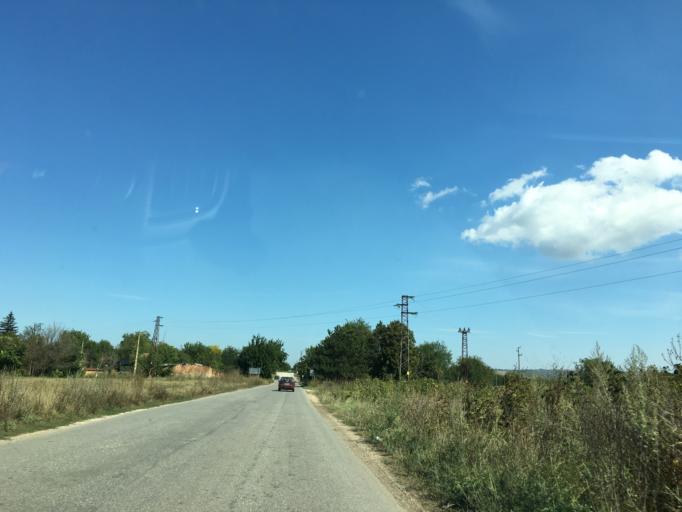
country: RO
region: Olt
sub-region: Comuna Orlea
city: Orlea
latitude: 43.6344
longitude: 24.3930
